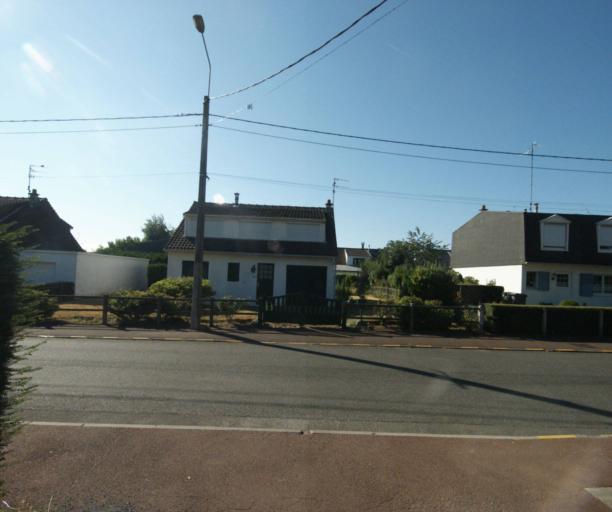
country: FR
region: Nord-Pas-de-Calais
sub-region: Departement du Nord
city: Mouvaux
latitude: 50.7052
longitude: 3.1511
